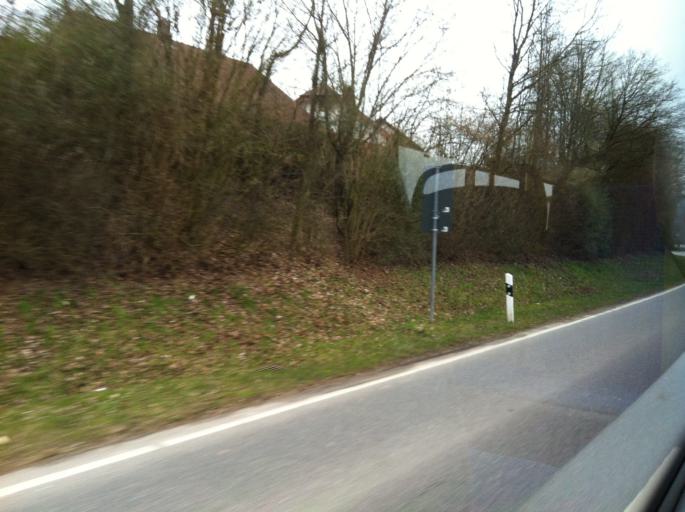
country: DE
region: Baden-Wuerttemberg
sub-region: Karlsruhe Region
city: Fahrenbach
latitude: 49.4269
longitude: 9.1544
